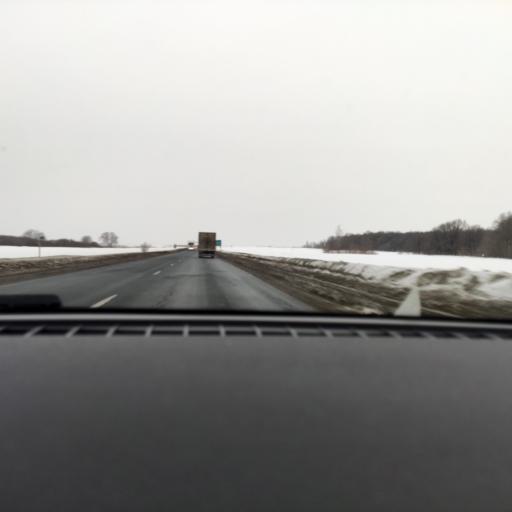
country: RU
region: Samara
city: Petra-Dubrava
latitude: 53.3287
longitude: 50.4537
